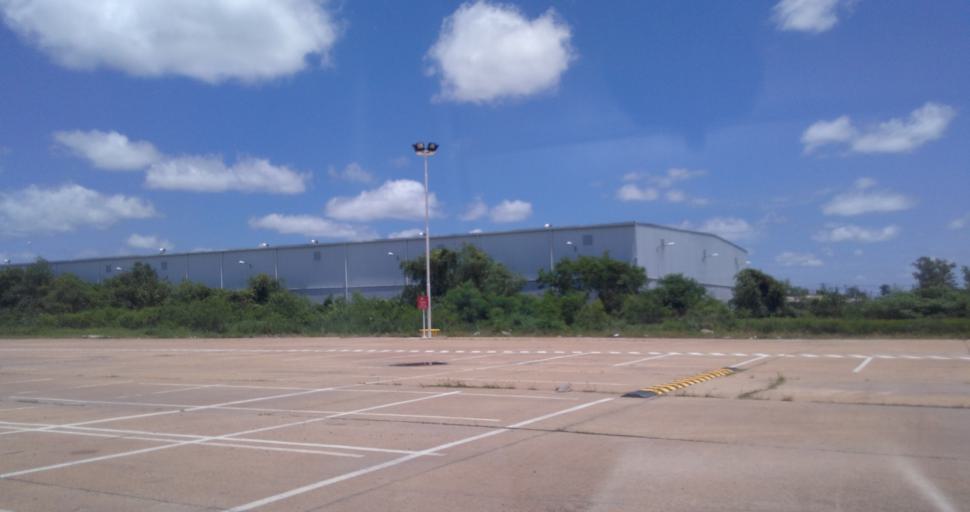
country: AR
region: Chaco
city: Resistencia
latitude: -27.4116
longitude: -58.9685
